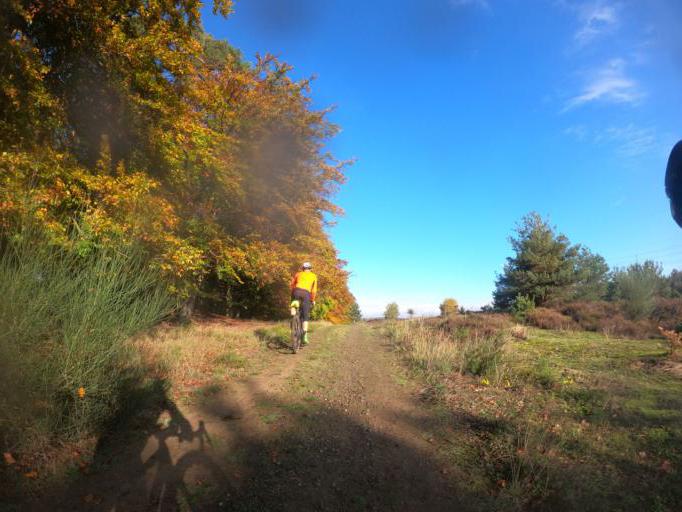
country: DE
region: Hesse
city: Kelsterbach
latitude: 50.0210
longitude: 8.5061
